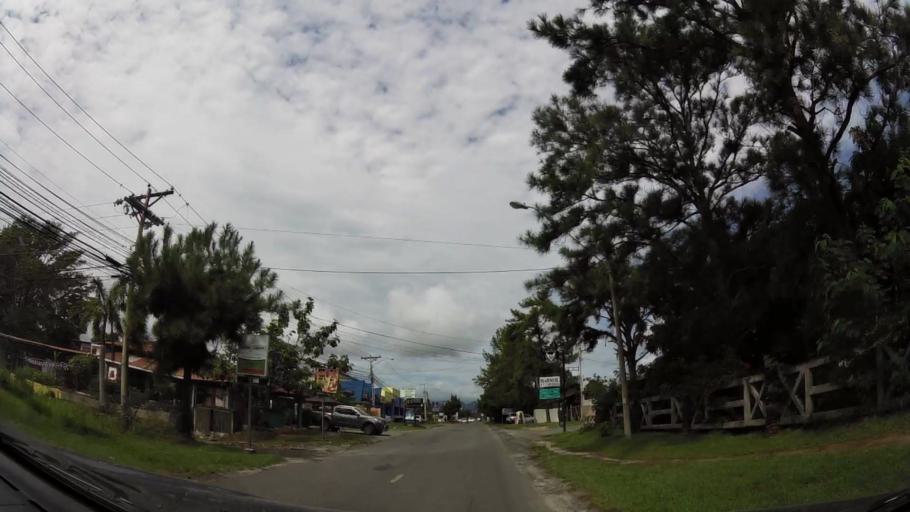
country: PA
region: Panama
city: Nueva Gorgona
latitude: 8.5400
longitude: -79.9098
